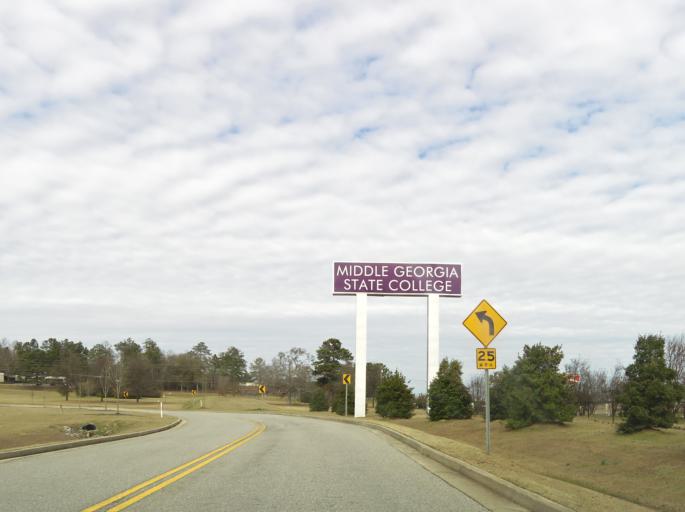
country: US
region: Georgia
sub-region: Bibb County
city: West Point
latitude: 32.8156
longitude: -83.7290
